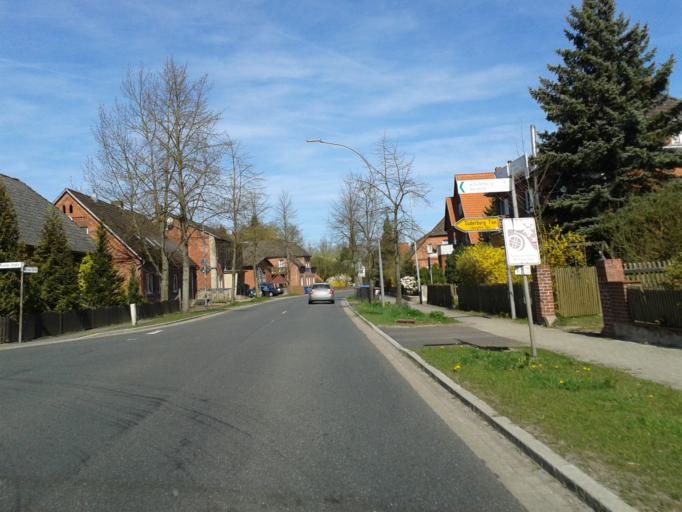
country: DE
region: Lower Saxony
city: Gerdau
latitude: 52.9630
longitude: 10.4172
